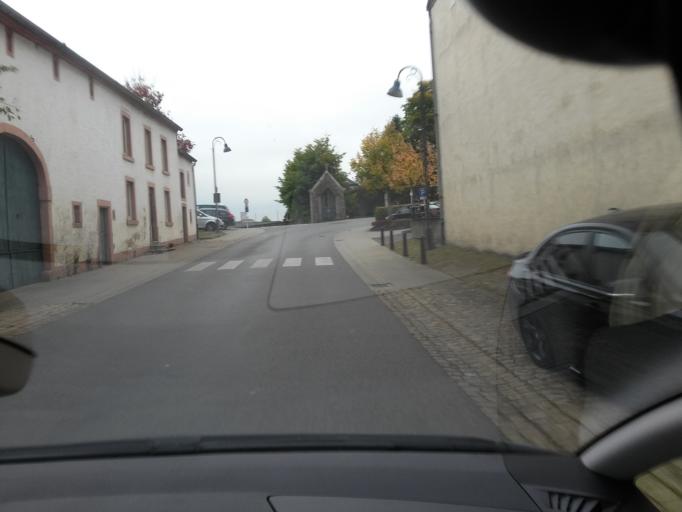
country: LU
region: Diekirch
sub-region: Canton de Redange
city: Beckerich
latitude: 49.7305
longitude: 5.8828
